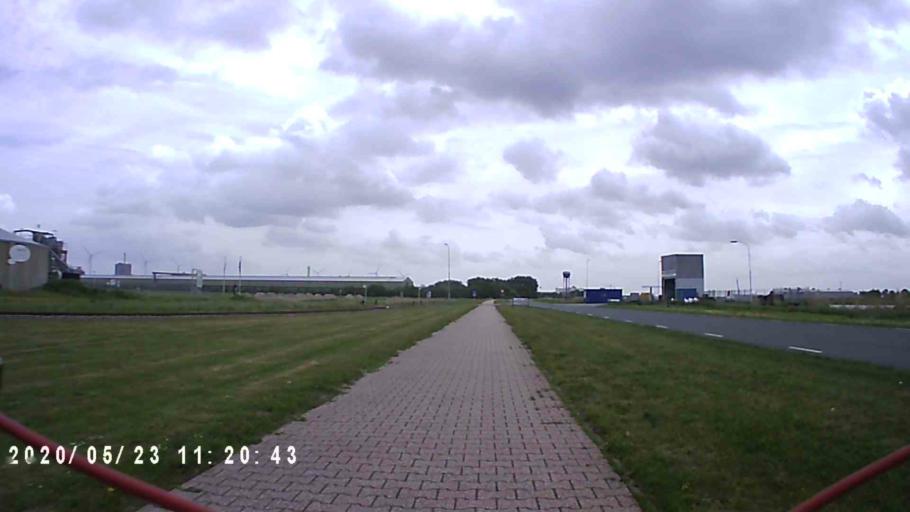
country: NL
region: Groningen
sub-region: Gemeente Delfzijl
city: Delfzijl
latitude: 53.3070
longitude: 6.9658
